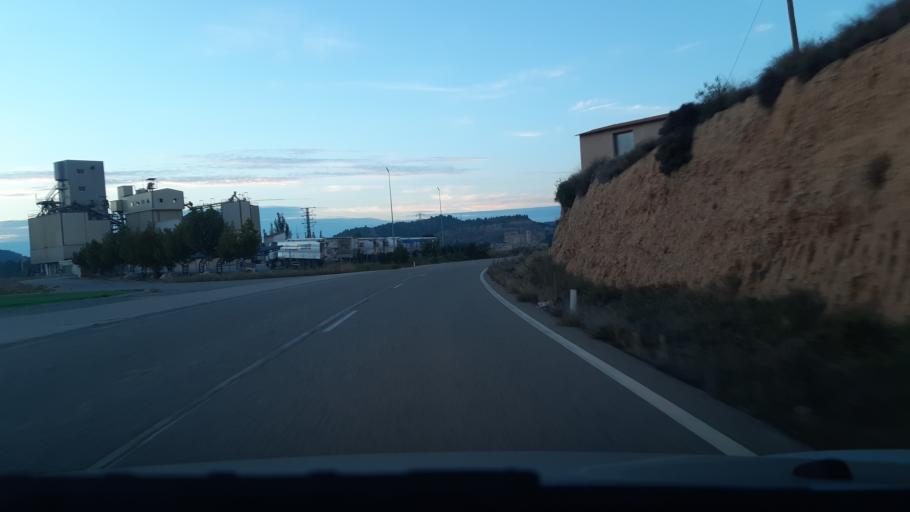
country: ES
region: Aragon
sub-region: Provincia de Teruel
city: Valderrobres
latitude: 40.8651
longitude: 0.1640
